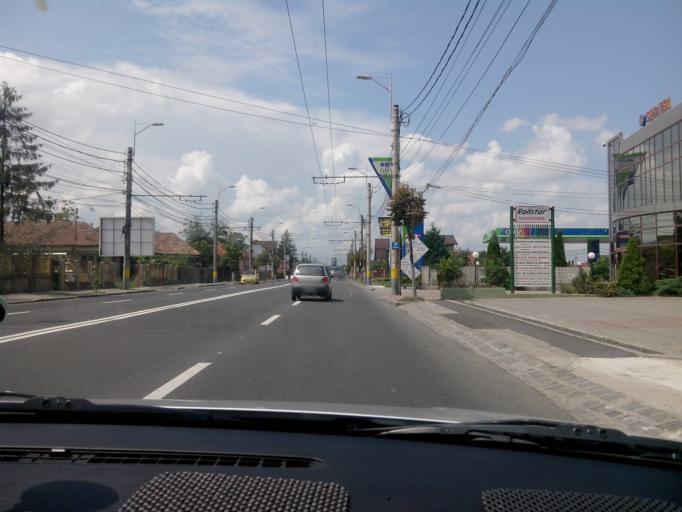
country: RO
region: Cluj
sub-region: Comuna Apahida
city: Sannicoara
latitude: 46.7806
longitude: 23.6729
